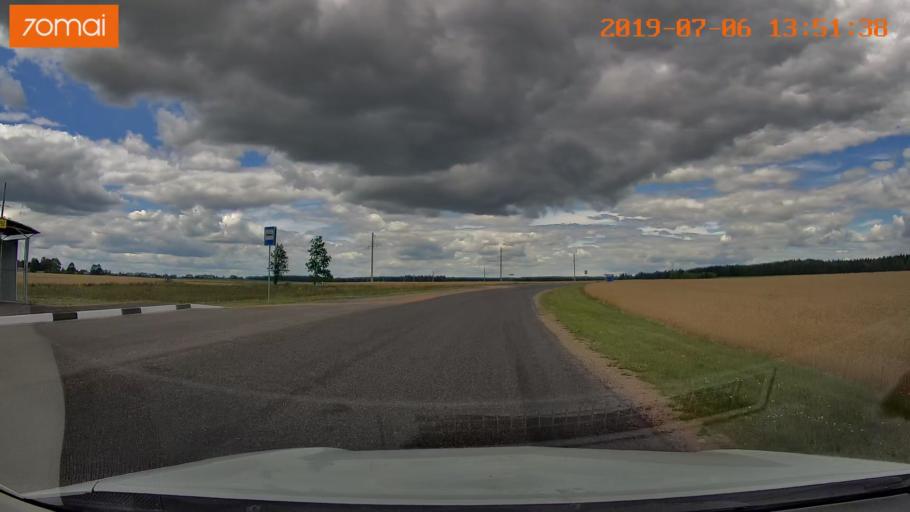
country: BY
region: Minsk
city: Ivyanyets
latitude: 53.7104
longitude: 26.8292
